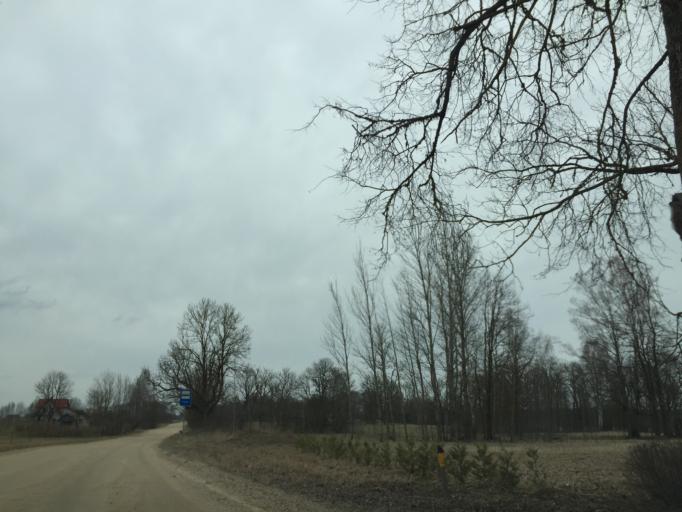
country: LV
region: Livani
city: Livani
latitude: 56.2956
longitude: 26.1732
